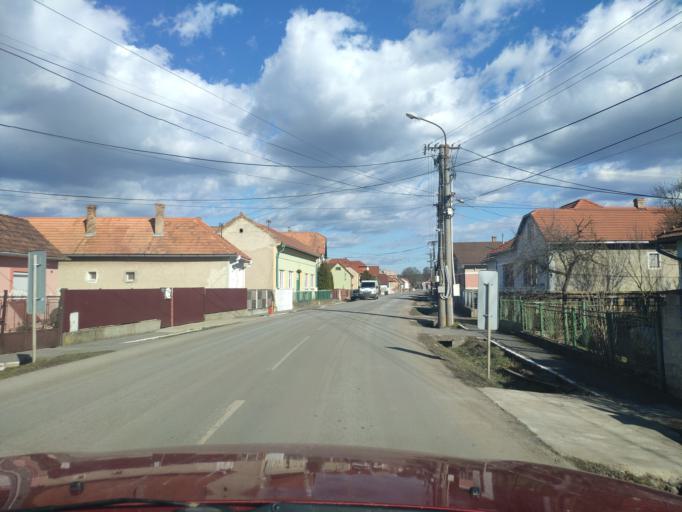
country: HU
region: Borsod-Abauj-Zemplen
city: Putnok
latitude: 48.3172
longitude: 20.3306
